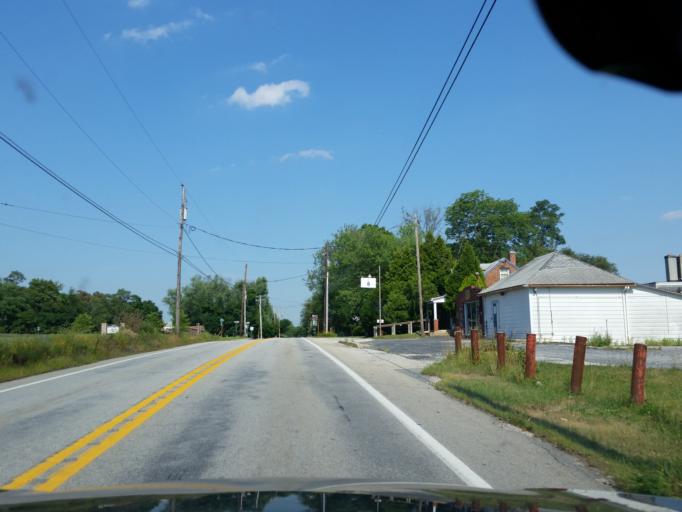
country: US
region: Pennsylvania
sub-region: Cumberland County
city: Mechanicsburg
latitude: 40.2869
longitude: -77.0090
